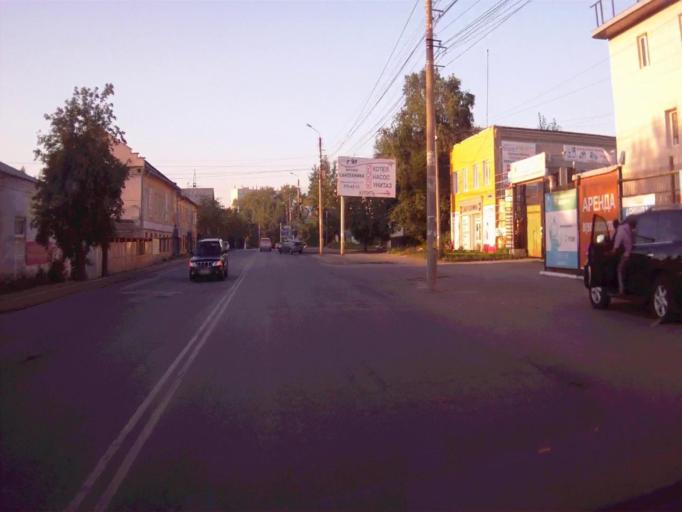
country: RU
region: Chelyabinsk
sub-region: Gorod Chelyabinsk
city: Chelyabinsk
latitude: 55.1662
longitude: 61.4347
